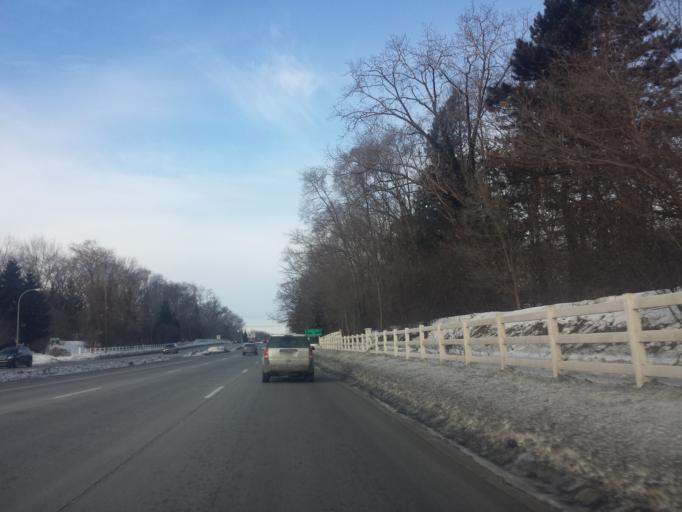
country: US
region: Michigan
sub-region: Oakland County
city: Pontiac
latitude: 42.6032
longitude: -83.2816
